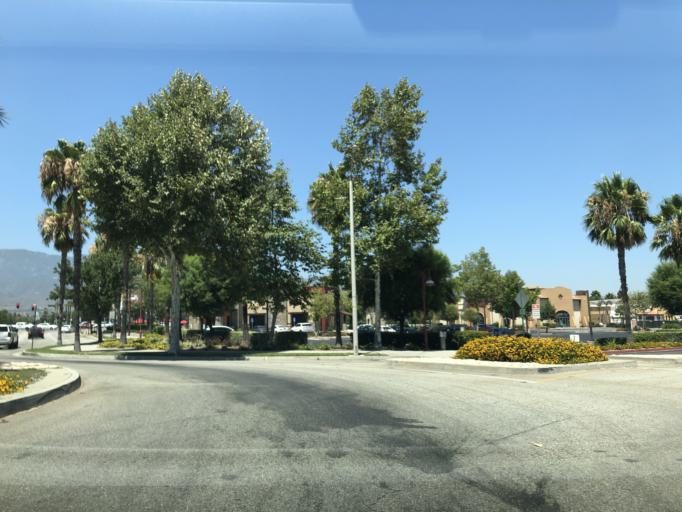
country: US
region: California
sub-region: San Bernardino County
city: Rancho Cucamonga
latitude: 34.1049
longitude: -117.5370
